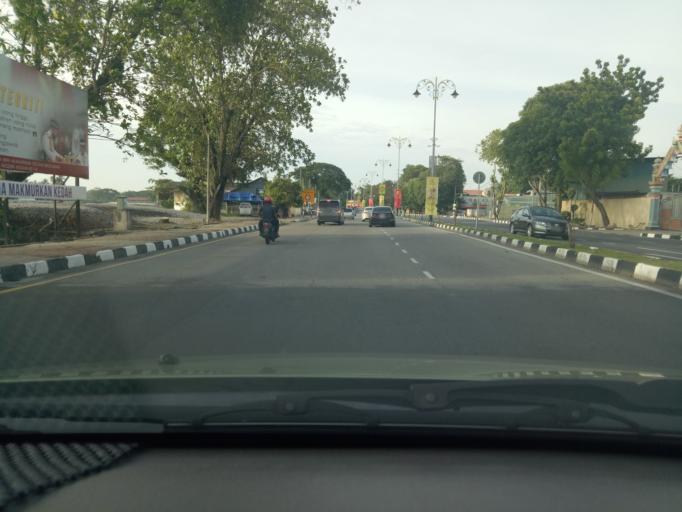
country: MY
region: Kedah
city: Alor Setar
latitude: 6.1376
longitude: 100.3699
